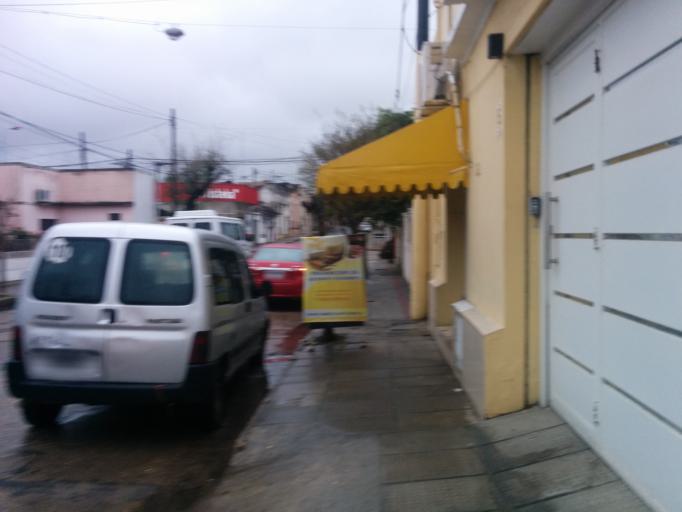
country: AR
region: Entre Rios
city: Concordia
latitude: -31.3876
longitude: -58.0144
